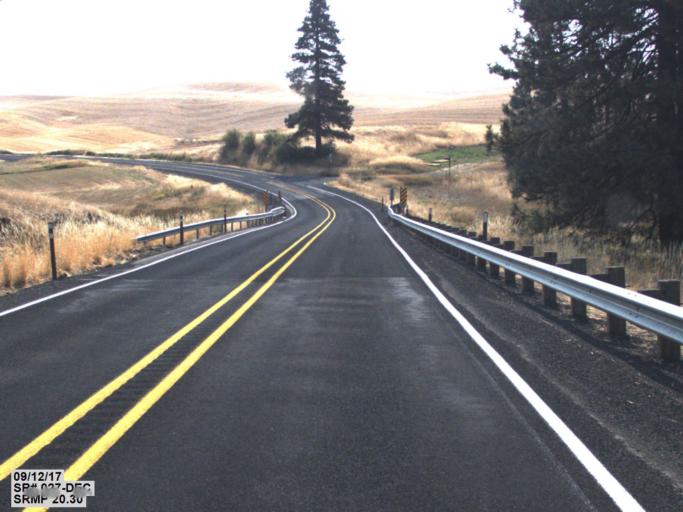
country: US
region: Washington
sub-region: Whitman County
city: Pullman
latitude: 46.9630
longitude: -117.1078
